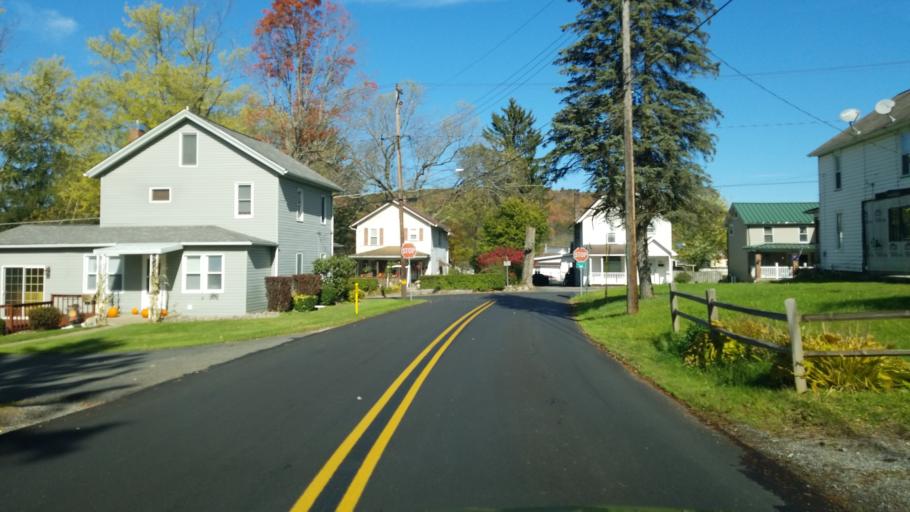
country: US
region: Pennsylvania
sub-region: Jefferson County
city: Brockway
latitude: 41.2463
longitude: -78.7959
